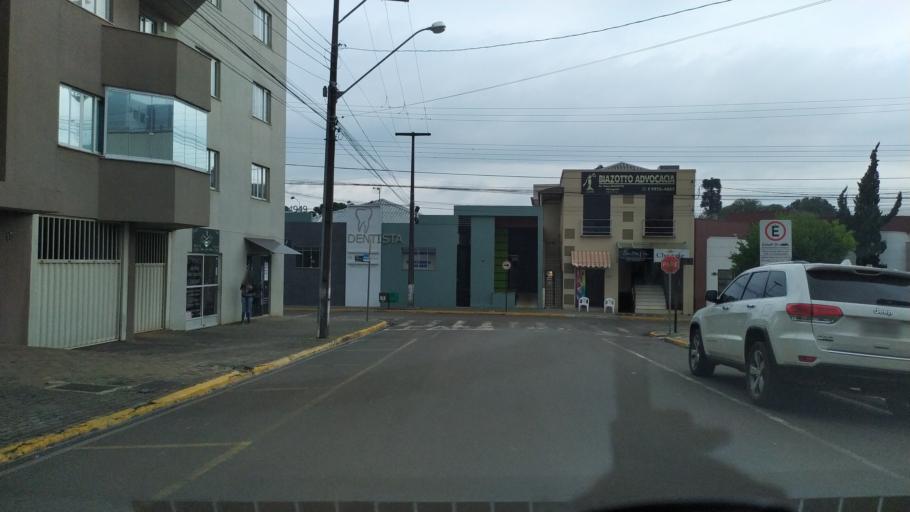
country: BR
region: Parana
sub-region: Palmas
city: Palmas
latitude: -26.4826
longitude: -51.9930
